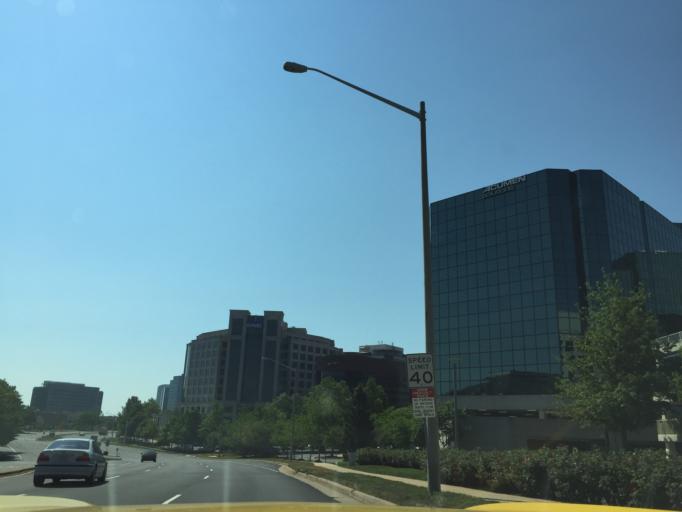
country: US
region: Virginia
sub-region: Fairfax County
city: Tysons Corner
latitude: 38.9259
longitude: -77.2308
